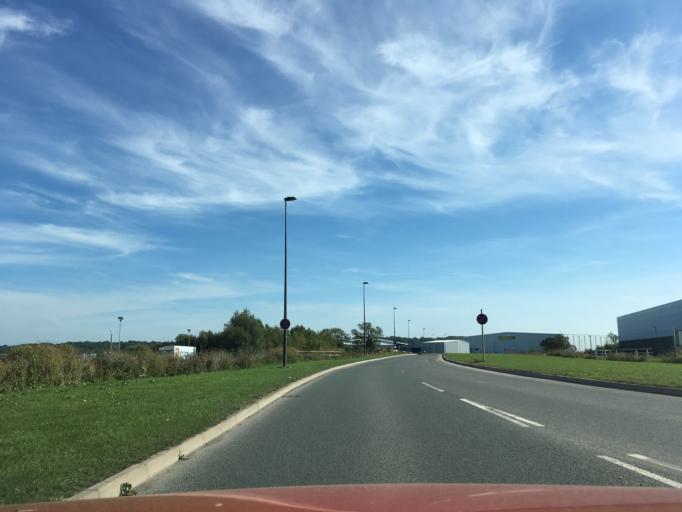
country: GB
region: England
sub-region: South Gloucestershire
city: Severn Beach
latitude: 51.5483
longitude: -2.6457
